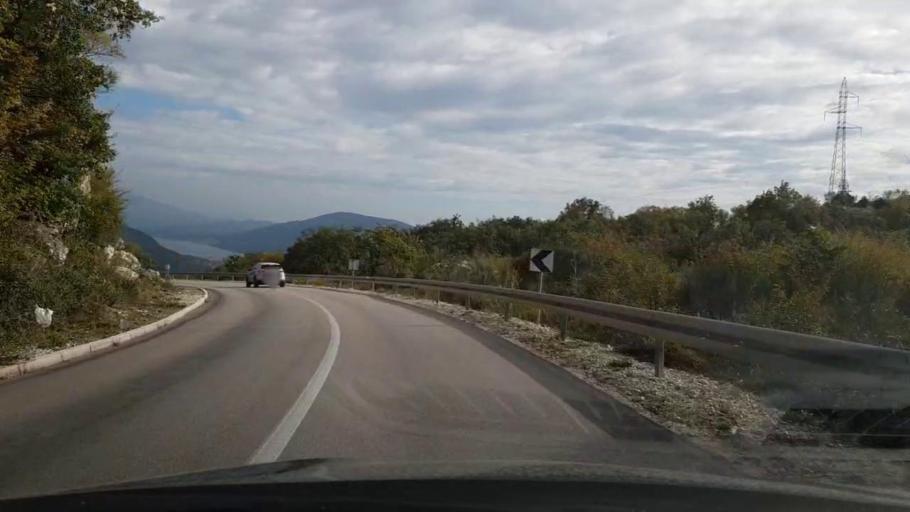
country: ME
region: Herceg Novi
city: Herceg-Novi
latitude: 42.4739
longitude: 18.5290
